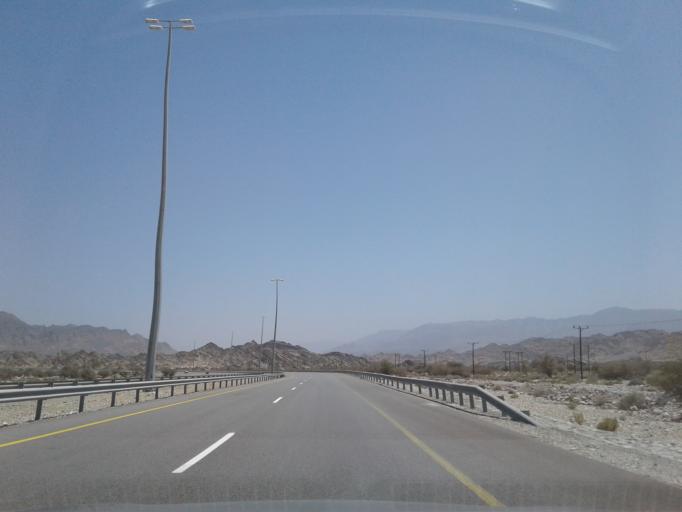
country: OM
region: Muhafazat Masqat
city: Muscat
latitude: 23.3370
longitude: 58.7038
